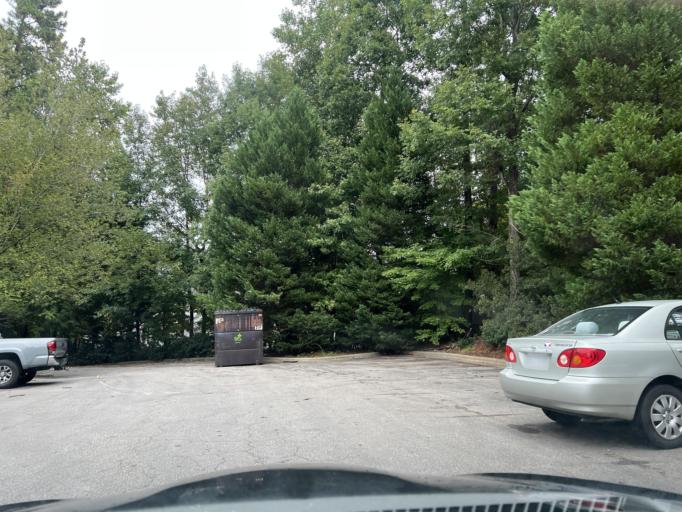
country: US
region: North Carolina
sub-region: Wake County
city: West Raleigh
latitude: 35.7488
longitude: -78.6939
